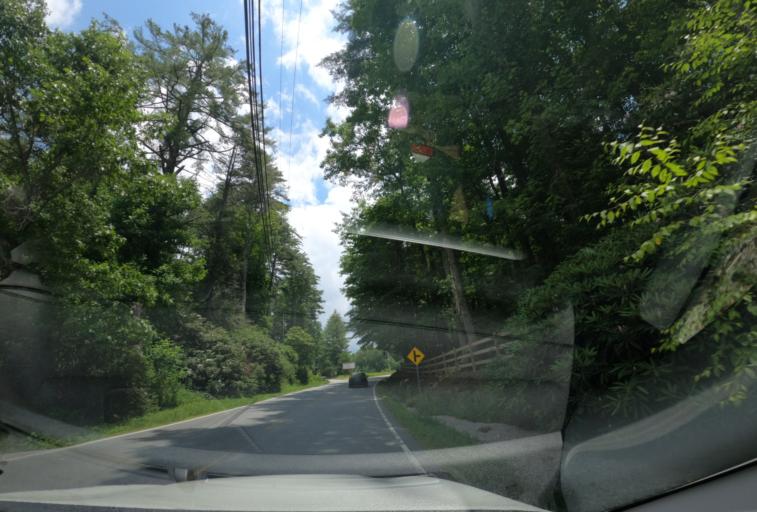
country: US
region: North Carolina
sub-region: Jackson County
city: Cullowhee
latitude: 35.1126
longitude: -83.1135
